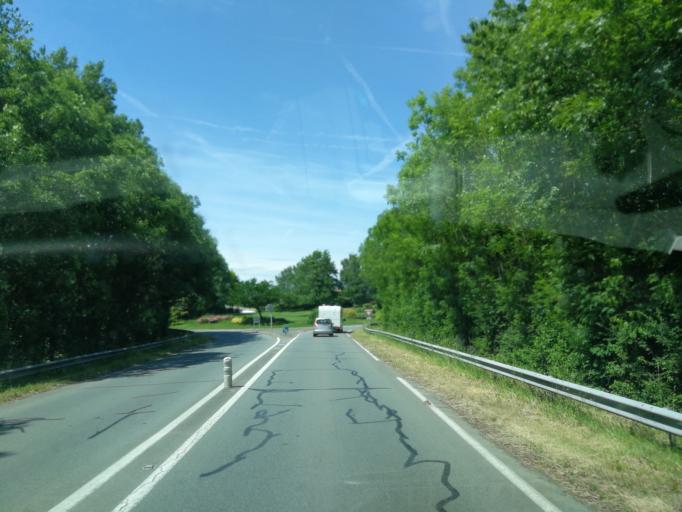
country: FR
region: Pays de la Loire
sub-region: Departement de la Vendee
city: La Tardiere
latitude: 46.6626
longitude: -0.7269
